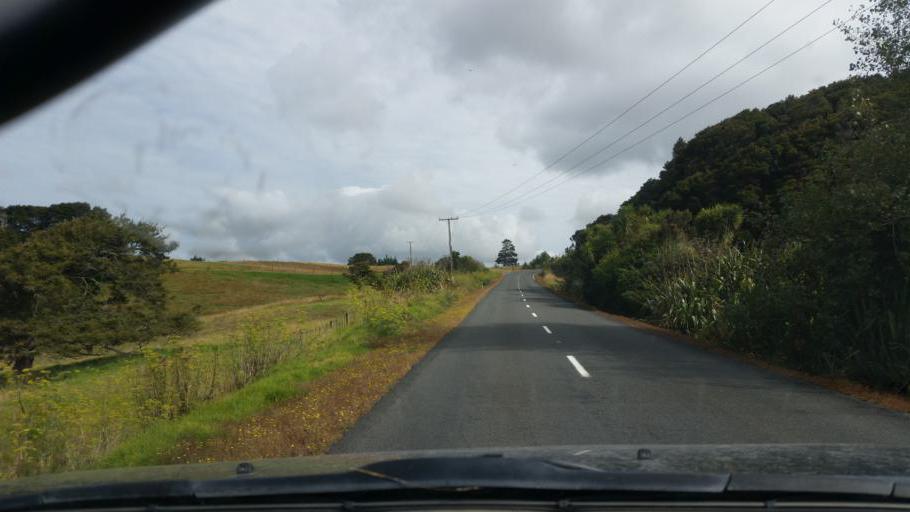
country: NZ
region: Northland
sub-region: Kaipara District
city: Dargaville
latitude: -35.9607
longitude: 173.9258
